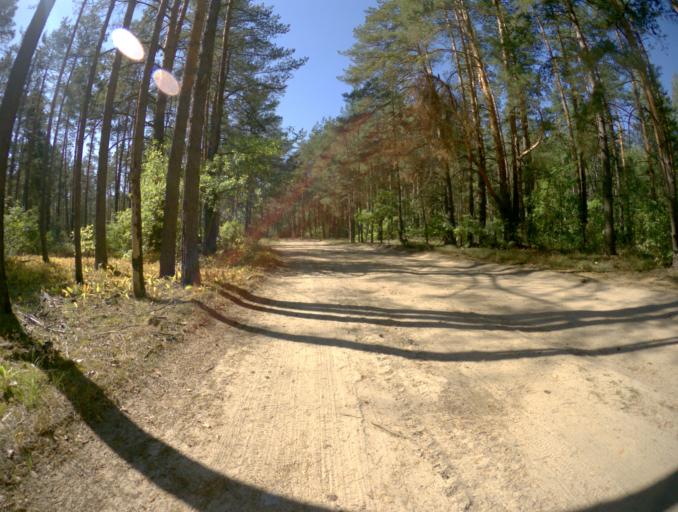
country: RU
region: Vladimir
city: Petushki
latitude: 55.8679
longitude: 39.3393
